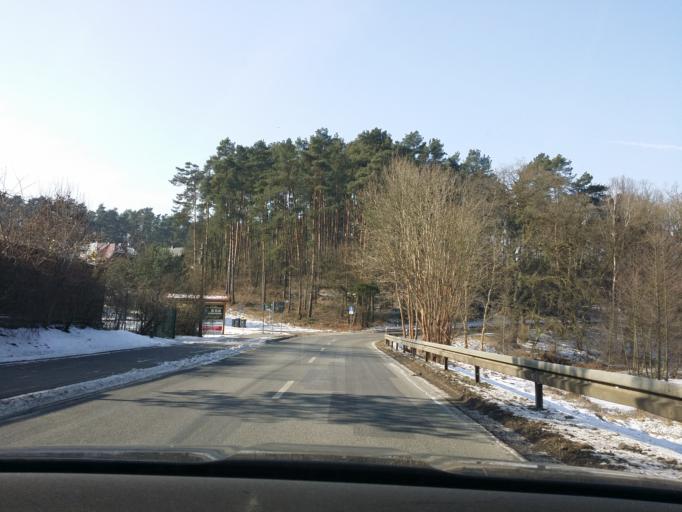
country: DE
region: Mecklenburg-Vorpommern
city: Rechlin
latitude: 53.2473
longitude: 12.6673
